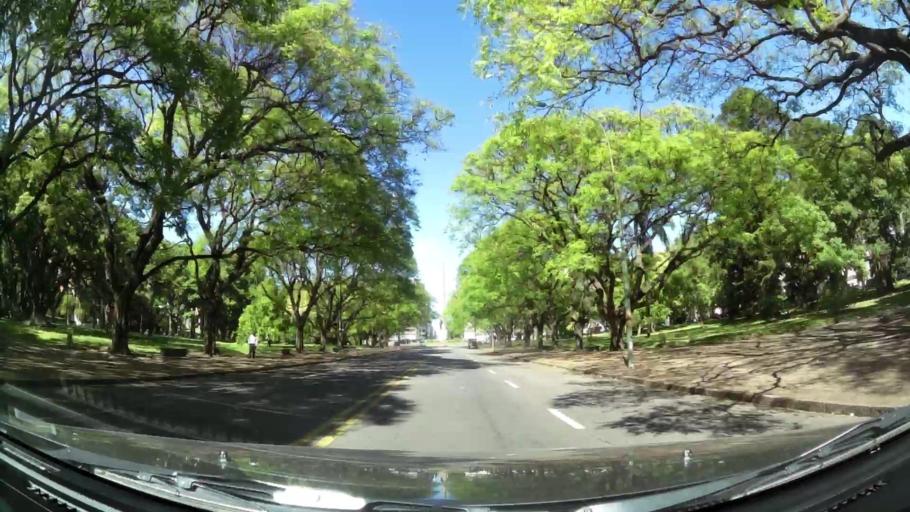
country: UY
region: Montevideo
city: Montevideo
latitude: -34.8966
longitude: -56.1624
